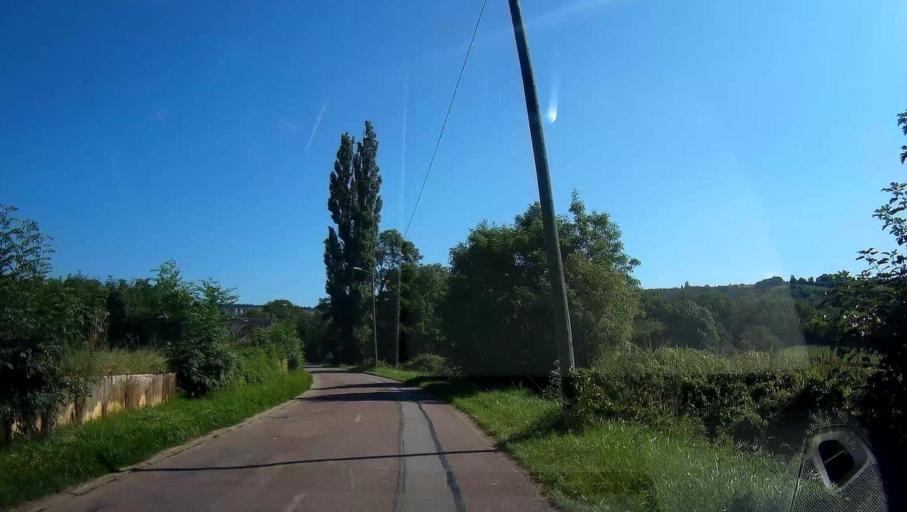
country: FR
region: Bourgogne
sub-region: Departement de la Cote-d'Or
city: Nolay
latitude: 46.9560
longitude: 4.6379
